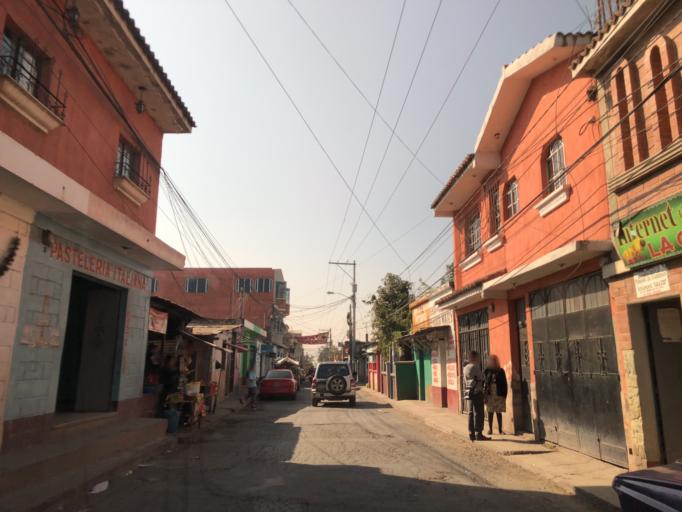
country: GT
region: Guatemala
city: Santa Catarina Pinula
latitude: 14.5423
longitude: -90.5246
